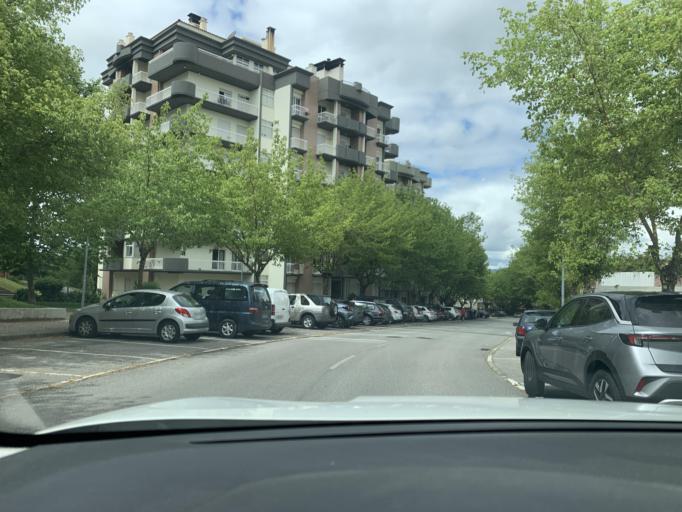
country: PT
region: Viseu
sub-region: Viseu
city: Viseu
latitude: 40.6586
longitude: -7.9273
